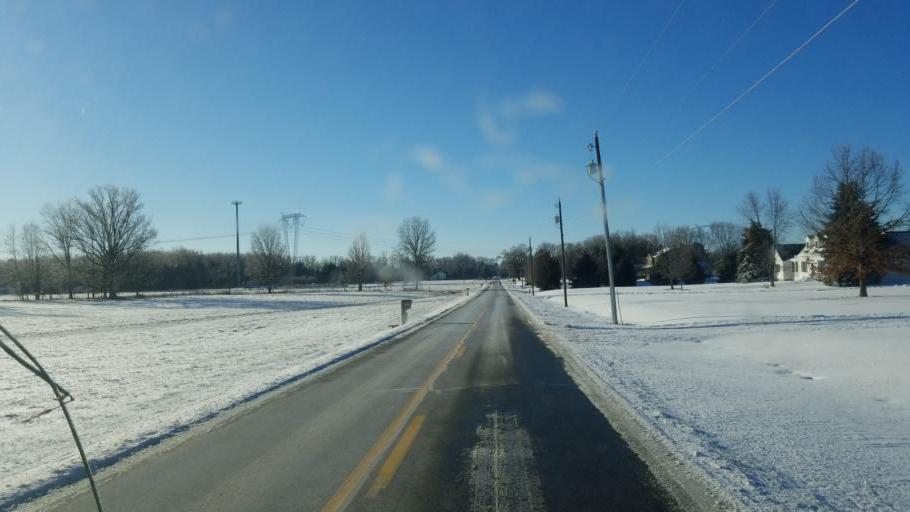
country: US
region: Ohio
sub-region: Delaware County
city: Sunbury
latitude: 40.2199
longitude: -82.9127
